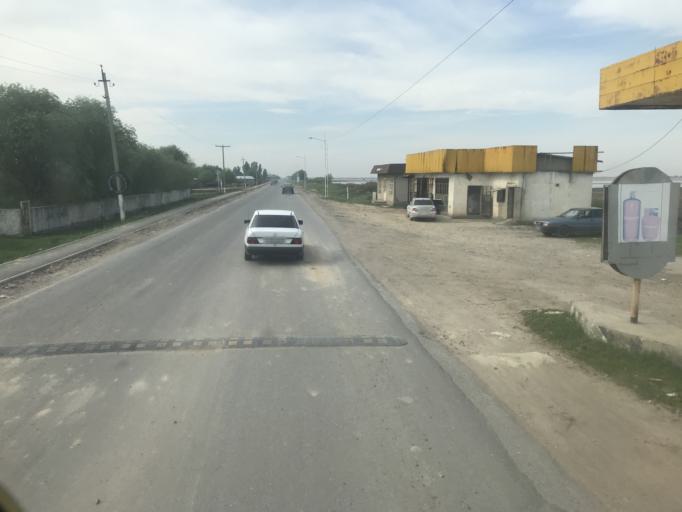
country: KZ
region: Ongtustik Qazaqstan
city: Asykata
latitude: 41.0024
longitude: 68.2138
